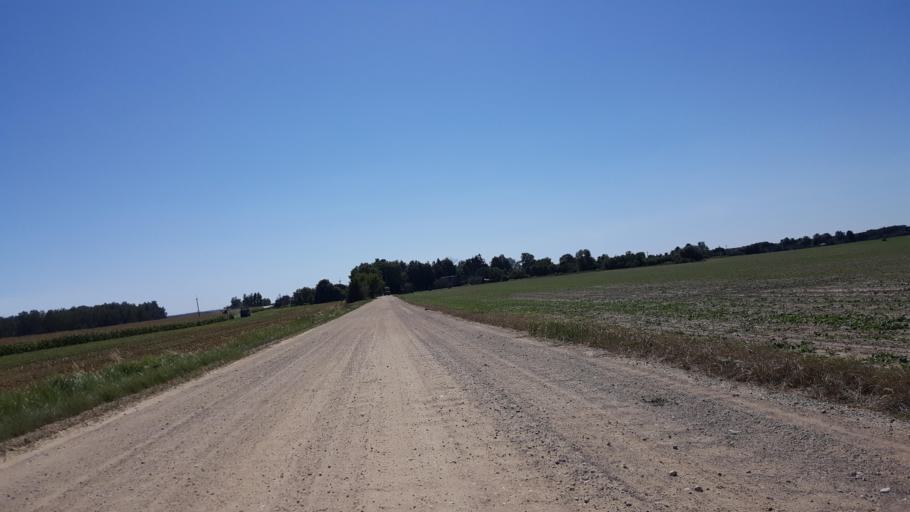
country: PL
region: Lublin Voivodeship
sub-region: Powiat bialski
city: Rokitno
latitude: 52.2183
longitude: 23.3984
